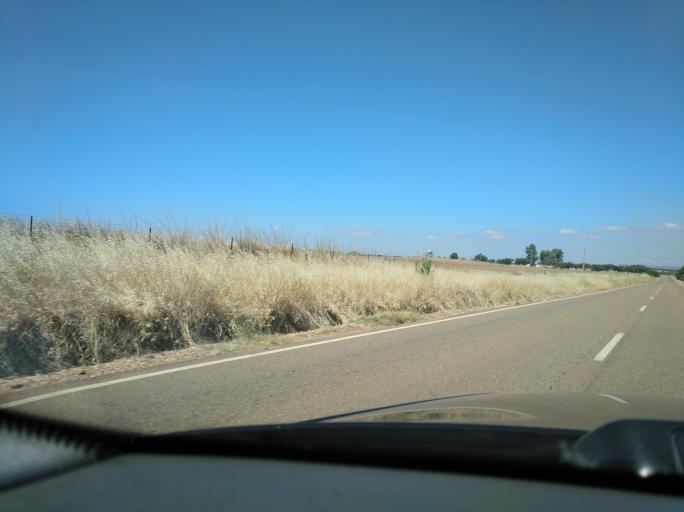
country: ES
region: Extremadura
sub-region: Provincia de Badajoz
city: Olivenza
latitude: 38.7007
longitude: -7.1530
